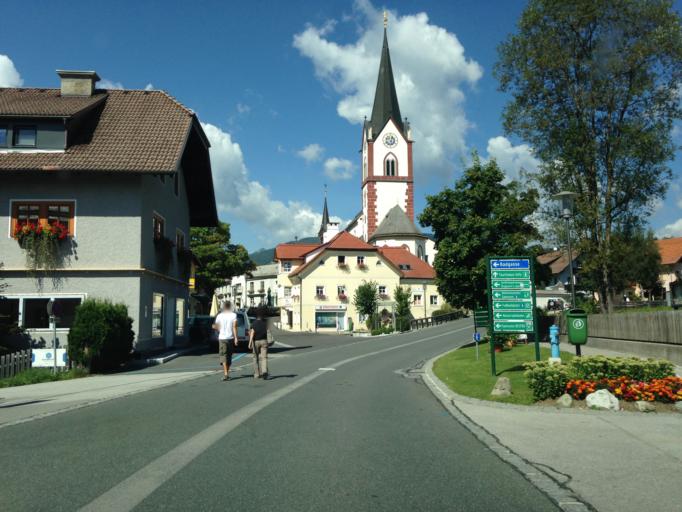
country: AT
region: Salzburg
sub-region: Politischer Bezirk Tamsweg
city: Mariapfarr
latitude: 47.1498
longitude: 13.7465
